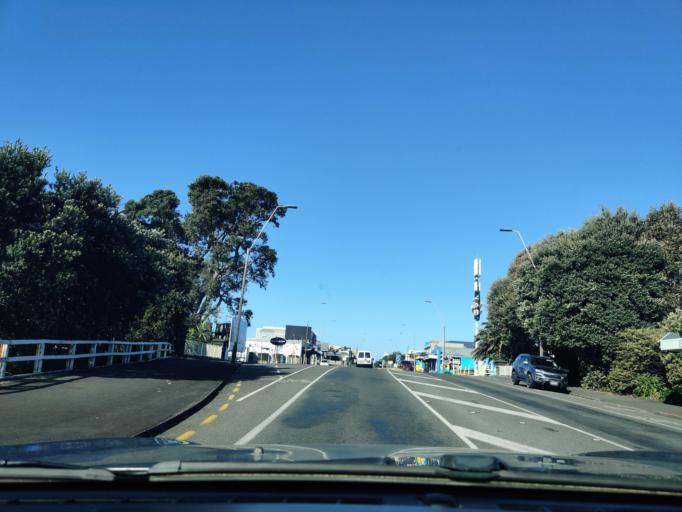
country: NZ
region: Taranaki
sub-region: New Plymouth District
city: New Plymouth
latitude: -39.0519
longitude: 174.0935
